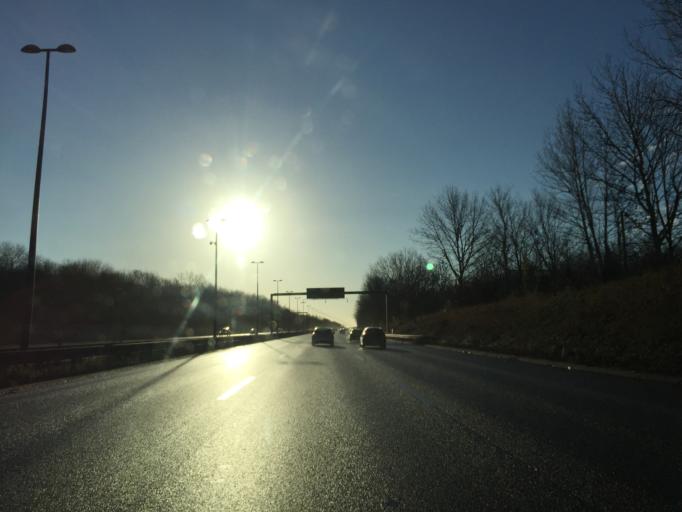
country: DK
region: Capital Region
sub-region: Brondby Kommune
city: Brondbyvester
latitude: 55.6641
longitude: 12.4229
